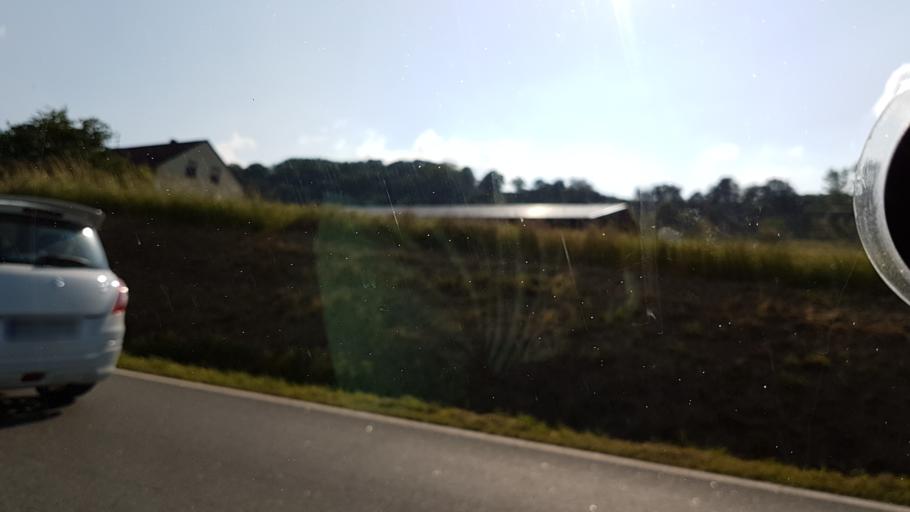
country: DE
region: Rheinland-Pfalz
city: Odenbach
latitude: 49.6929
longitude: 7.6542
